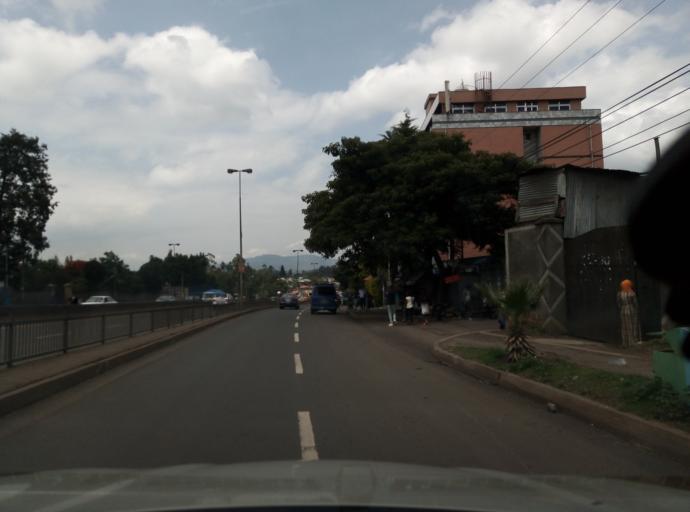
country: ET
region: Adis Abeba
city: Addis Ababa
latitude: 8.9953
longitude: 38.7181
